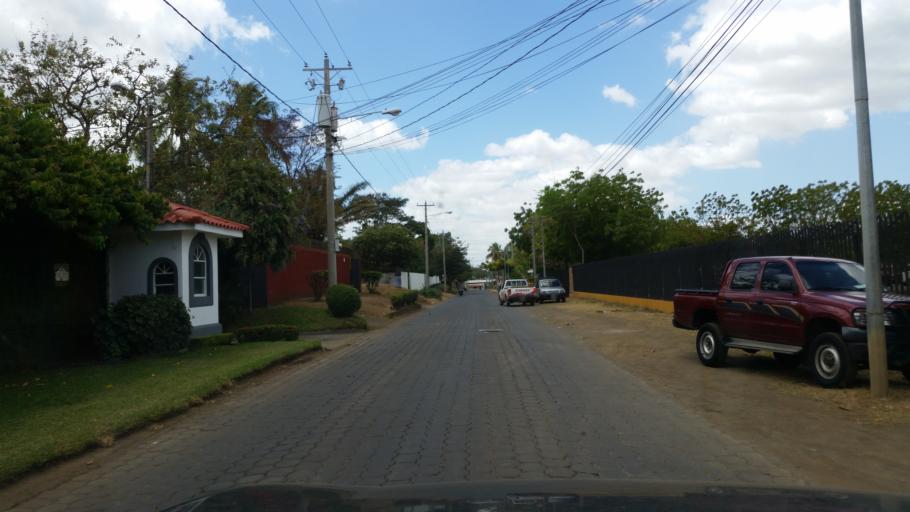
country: NI
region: Managua
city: Managua
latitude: 12.0988
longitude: -86.2290
